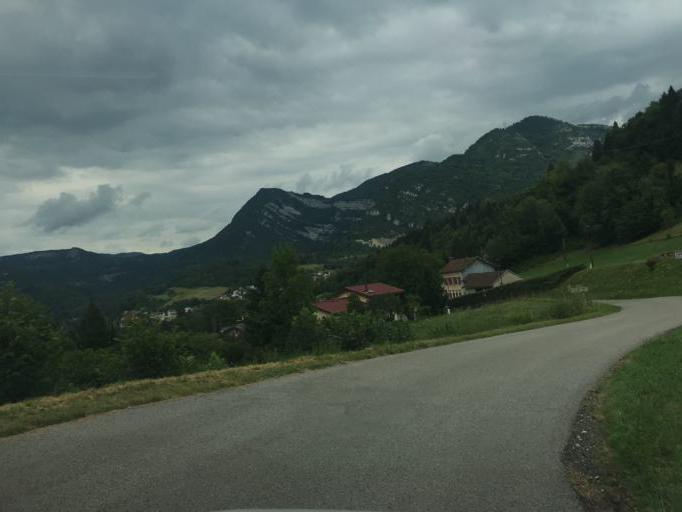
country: FR
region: Franche-Comte
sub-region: Departement du Jura
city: Saint-Claude
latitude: 46.3641
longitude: 5.8634
